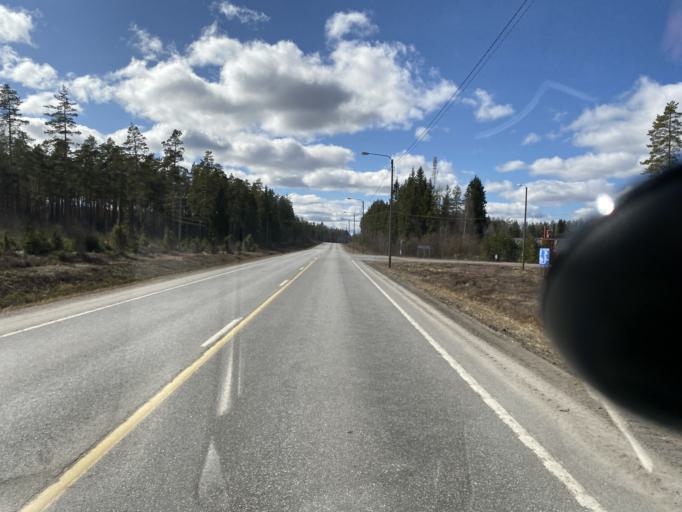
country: FI
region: Satakunta
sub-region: Rauma
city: Eura
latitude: 61.1413
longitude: 22.1886
